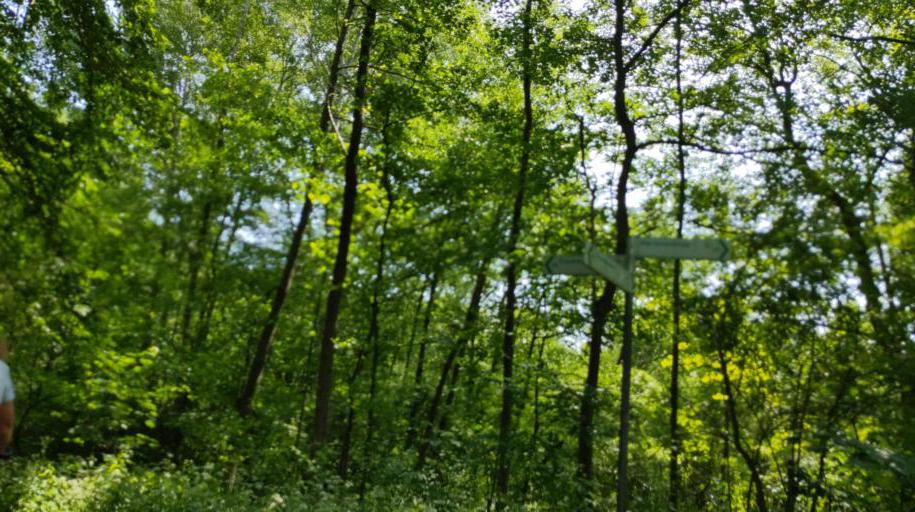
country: DE
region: Schleswig-Holstein
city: Fredeburg
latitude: 53.6713
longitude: 10.7169
